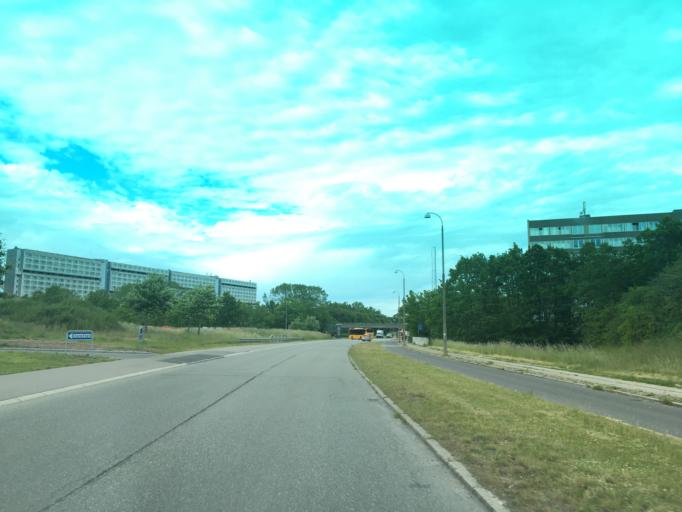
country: DK
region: Capital Region
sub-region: Hvidovre Kommune
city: Hvidovre
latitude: 55.6238
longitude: 12.4585
